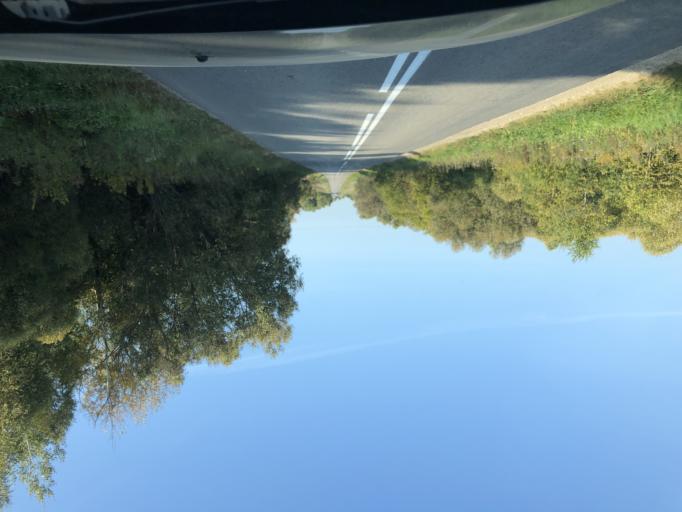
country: RU
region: Tula
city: Novogurovskiy
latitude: 54.3766
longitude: 37.3258
